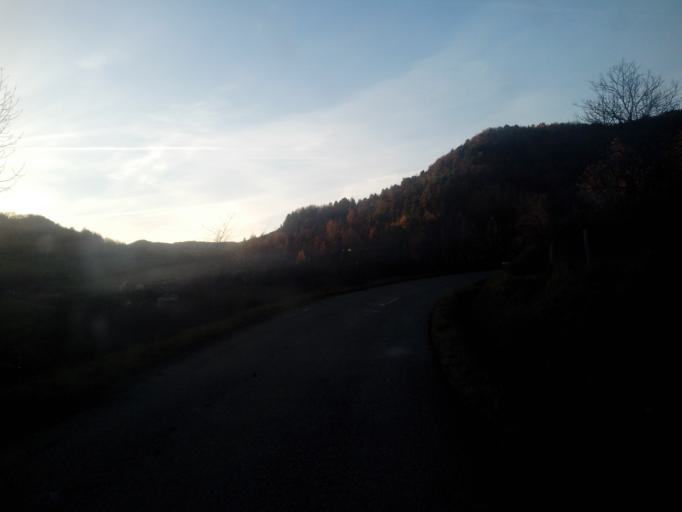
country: FR
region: Languedoc-Roussillon
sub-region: Departement de l'Aude
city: Quillan
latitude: 42.9363
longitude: 2.1172
